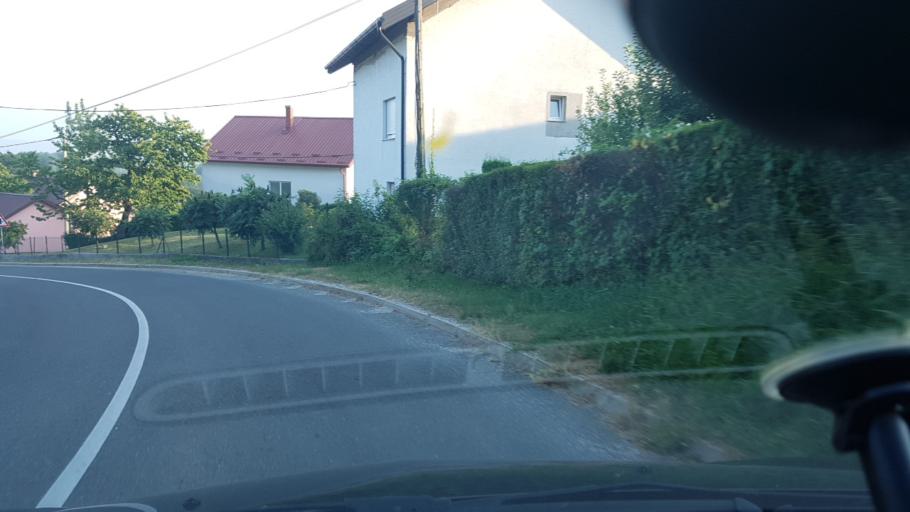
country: HR
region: Krapinsko-Zagorska
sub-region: Grad Krapina
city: Krapina
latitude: 46.1623
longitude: 15.8584
